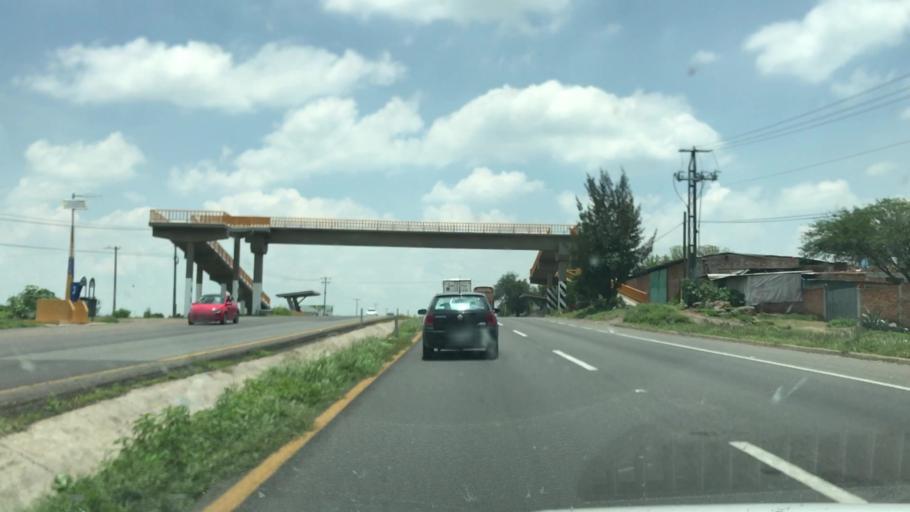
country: MX
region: Guanajuato
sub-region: Irapuato
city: Colonia Morelos de Guadalupe de Rivera
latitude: 20.5808
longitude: -101.4340
